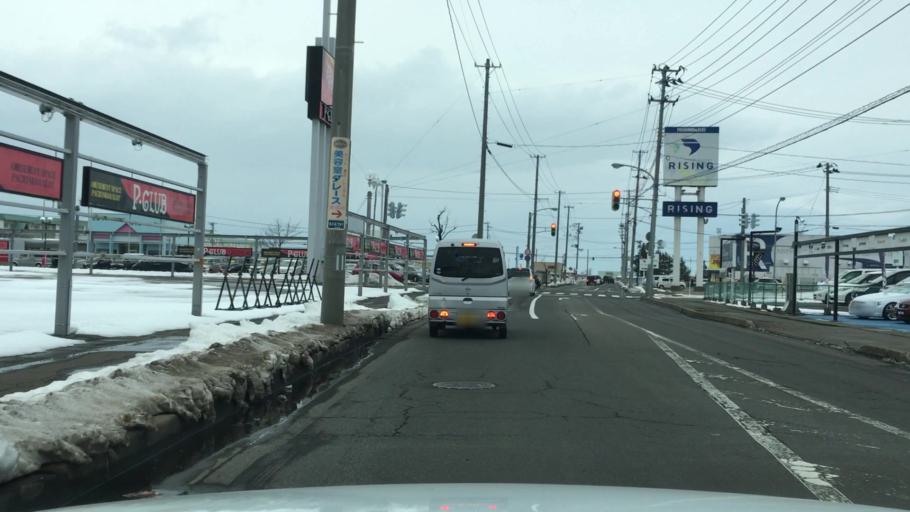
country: JP
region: Aomori
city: Hirosaki
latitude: 40.6103
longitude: 140.5043
